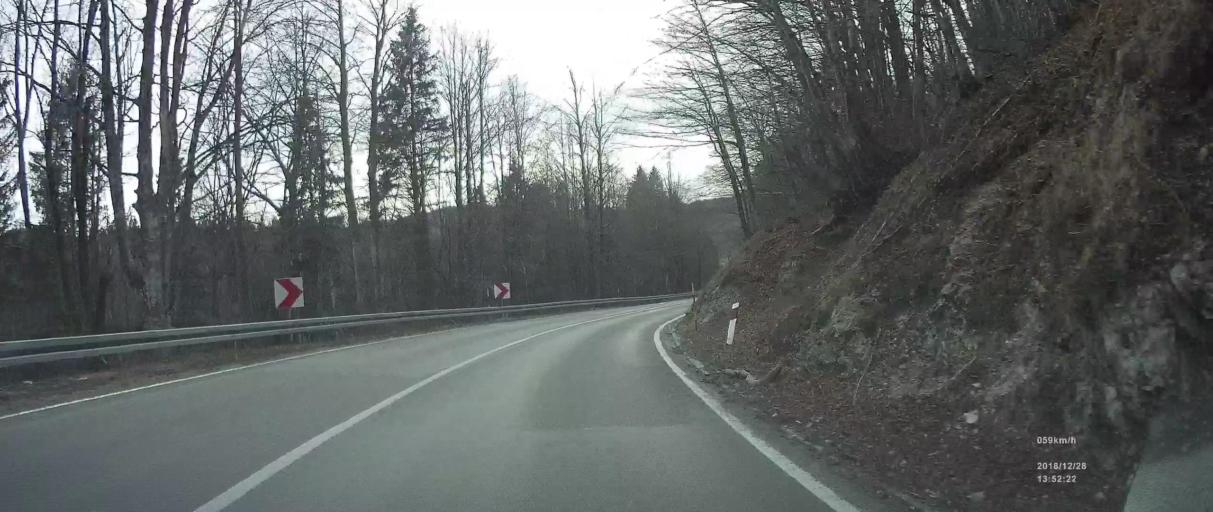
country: HR
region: Primorsko-Goranska
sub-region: Grad Delnice
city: Delnice
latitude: 45.3910
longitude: 14.8471
